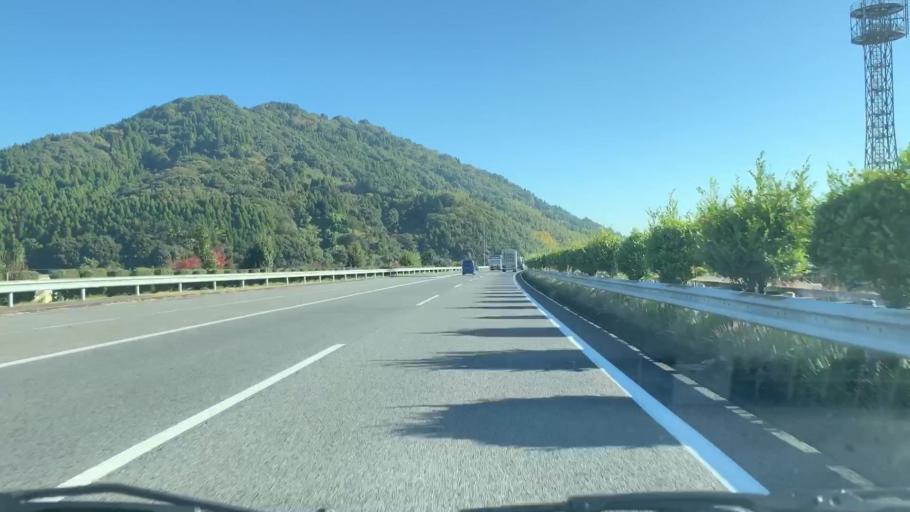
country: JP
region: Saga Prefecture
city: Takeocho-takeo
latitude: 33.2687
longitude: 130.0921
